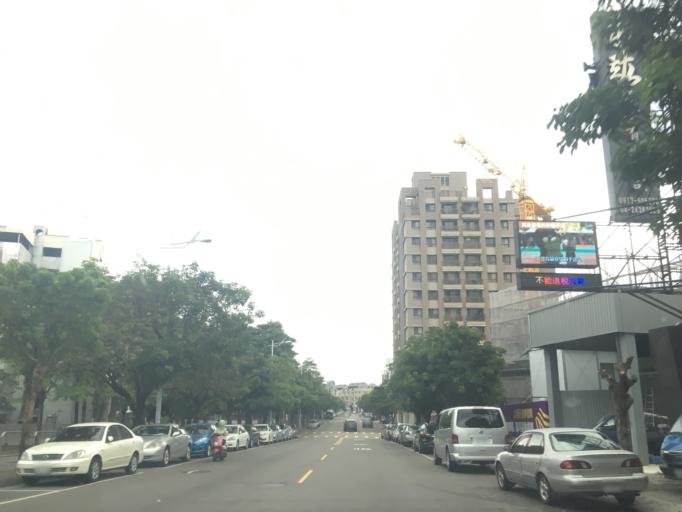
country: TW
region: Taiwan
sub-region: Taichung City
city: Taichung
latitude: 24.1622
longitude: 120.7213
